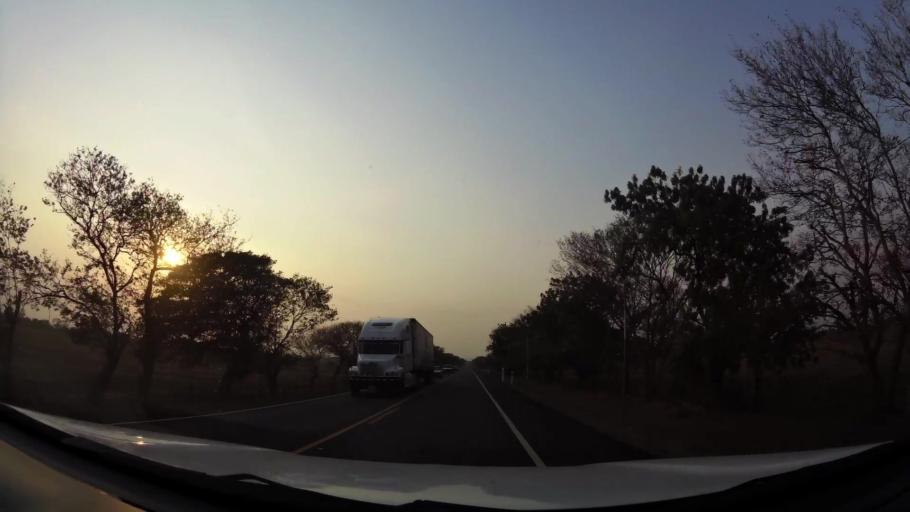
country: NI
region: Leon
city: Nagarote
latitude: 12.3027
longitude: -86.5979
